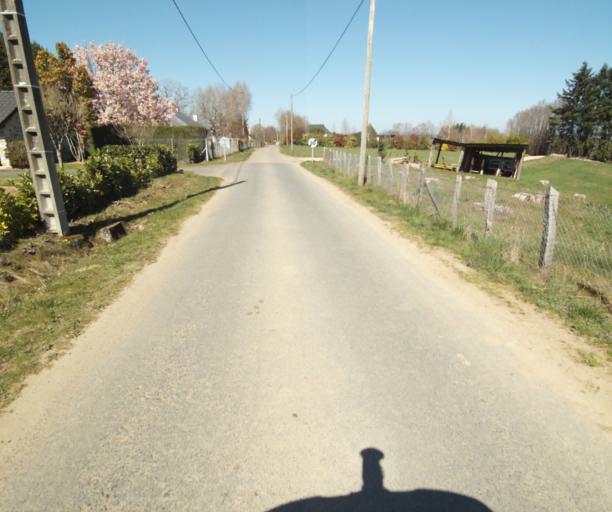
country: FR
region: Limousin
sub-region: Departement de la Correze
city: Saint-Clement
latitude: 45.3015
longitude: 1.6925
